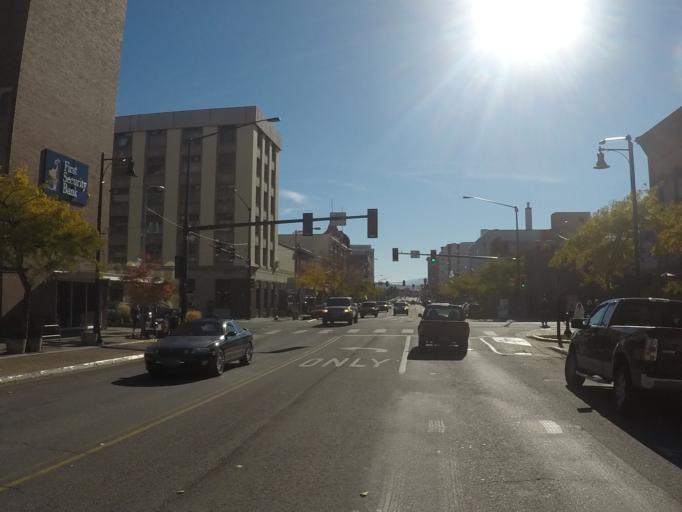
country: US
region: Montana
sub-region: Missoula County
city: Missoula
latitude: 46.8725
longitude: -113.9938
